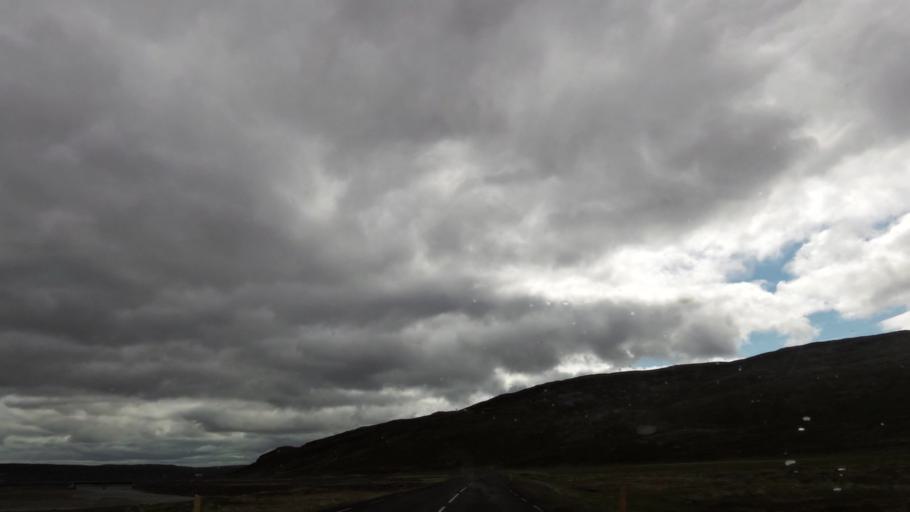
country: IS
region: West
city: Stykkisholmur
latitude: 65.7668
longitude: -21.7922
